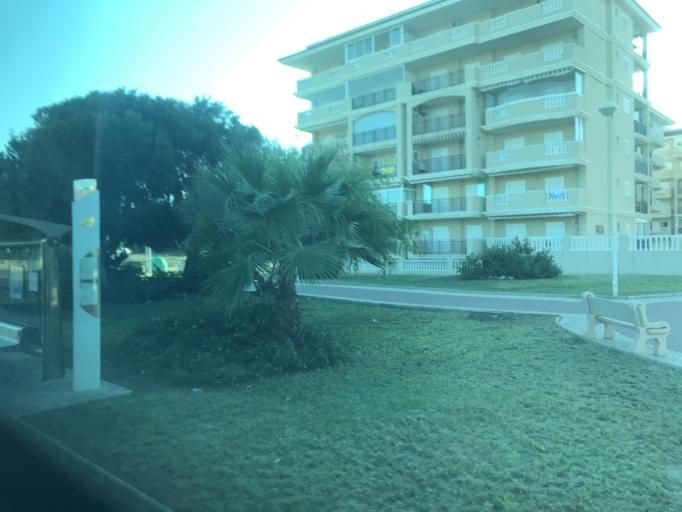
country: ES
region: Valencia
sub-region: Provincia de Alicante
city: Torrevieja
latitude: 38.0169
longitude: -0.6558
